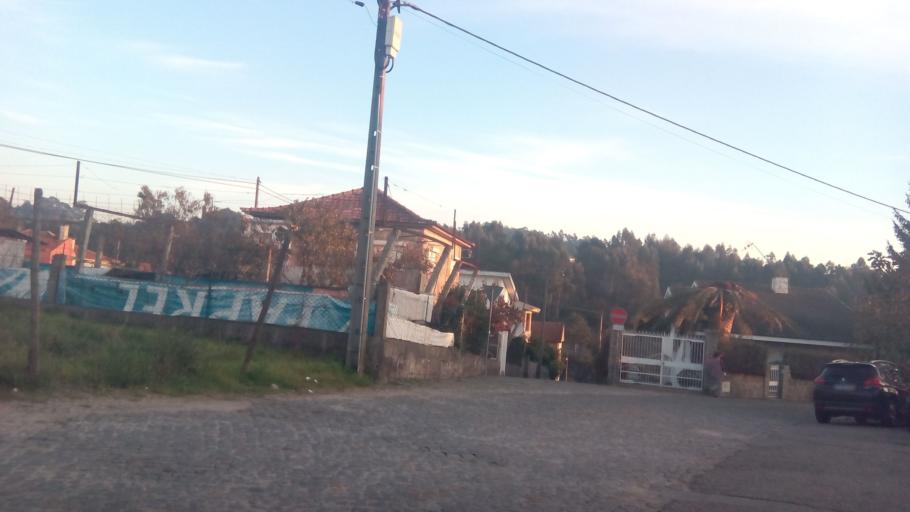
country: PT
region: Porto
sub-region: Paredes
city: Paredes
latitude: 41.1998
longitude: -8.3262
